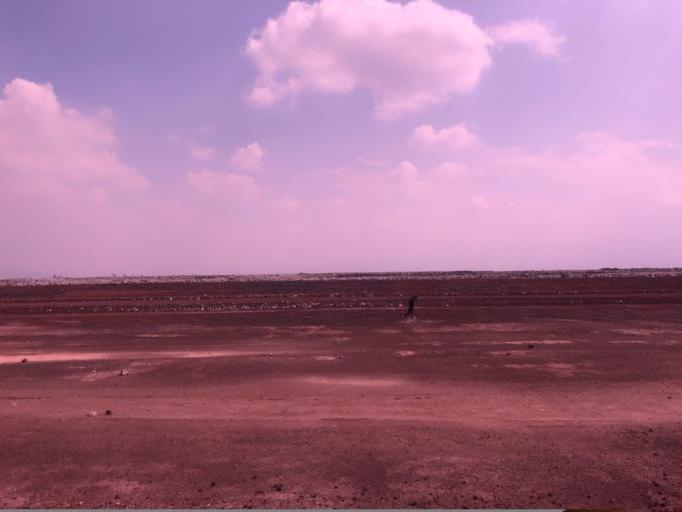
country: MX
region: Mexico
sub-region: Atenco
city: Colonia el Salado
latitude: 19.5259
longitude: -98.9946
